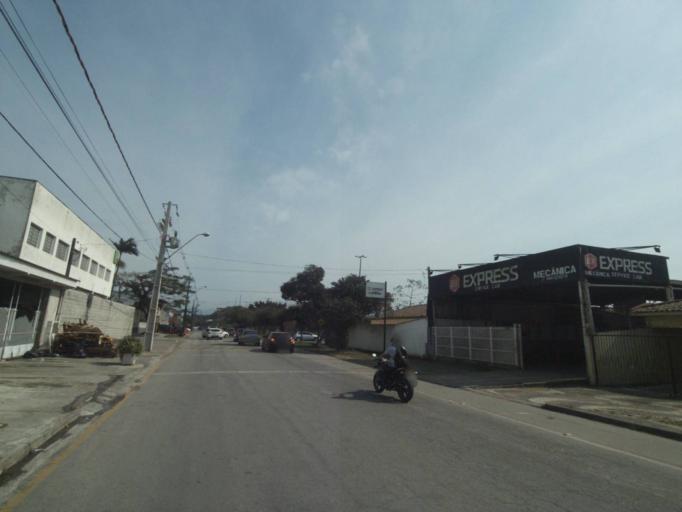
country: BR
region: Parana
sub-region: Paranagua
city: Paranagua
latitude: -25.5244
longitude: -48.5257
